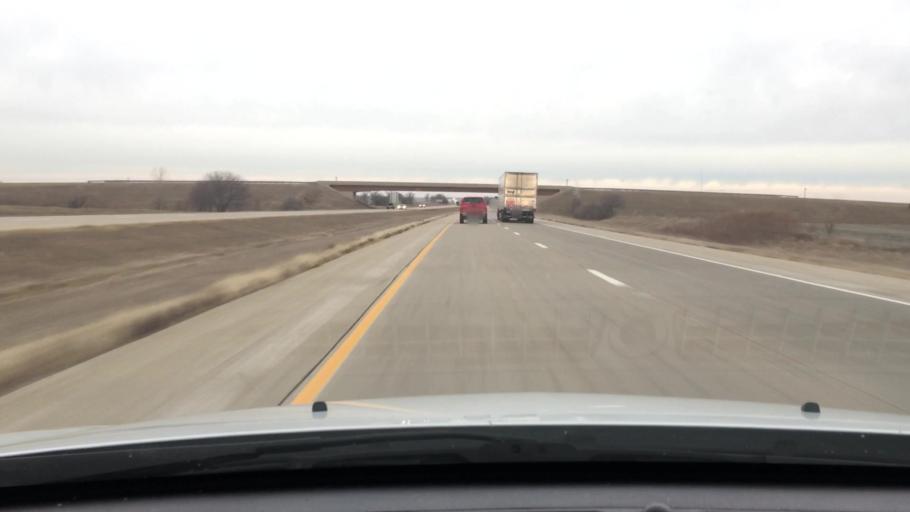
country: US
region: Illinois
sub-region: Woodford County
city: El Paso
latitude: 40.7493
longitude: -89.0346
